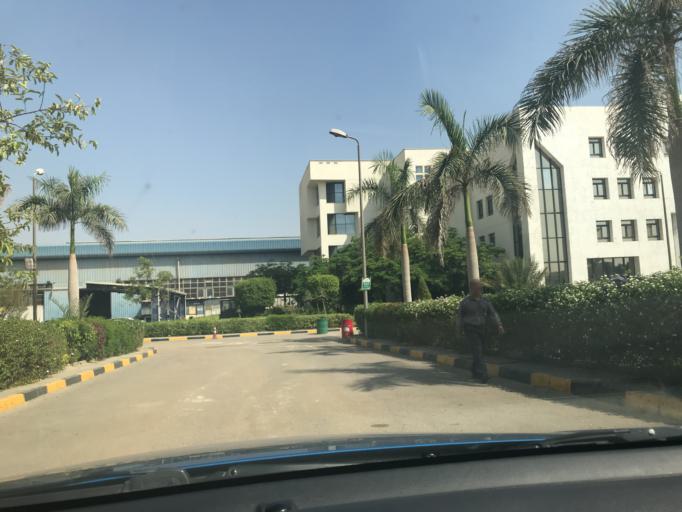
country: EG
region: Eastern Province
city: Bilbays
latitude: 30.2471
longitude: 31.7588
